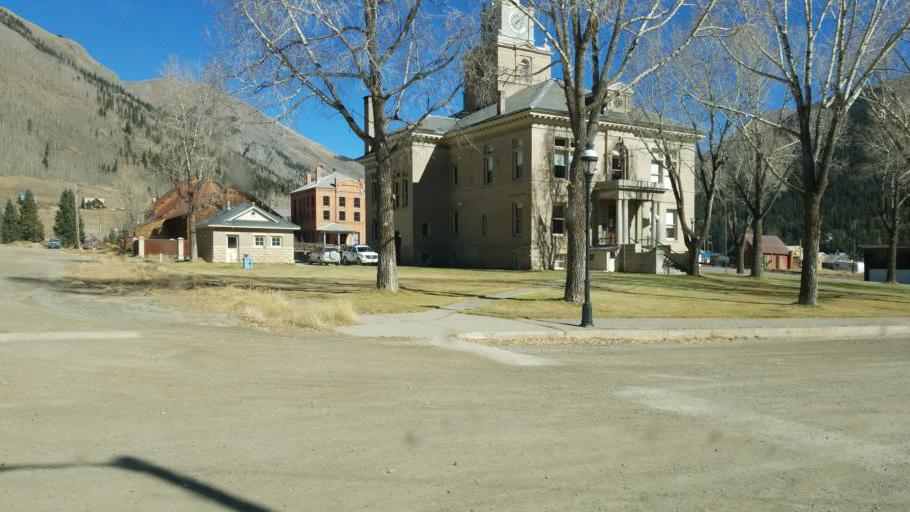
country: US
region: Colorado
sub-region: San Juan County
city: Silverton
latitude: 37.8146
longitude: -107.6629
